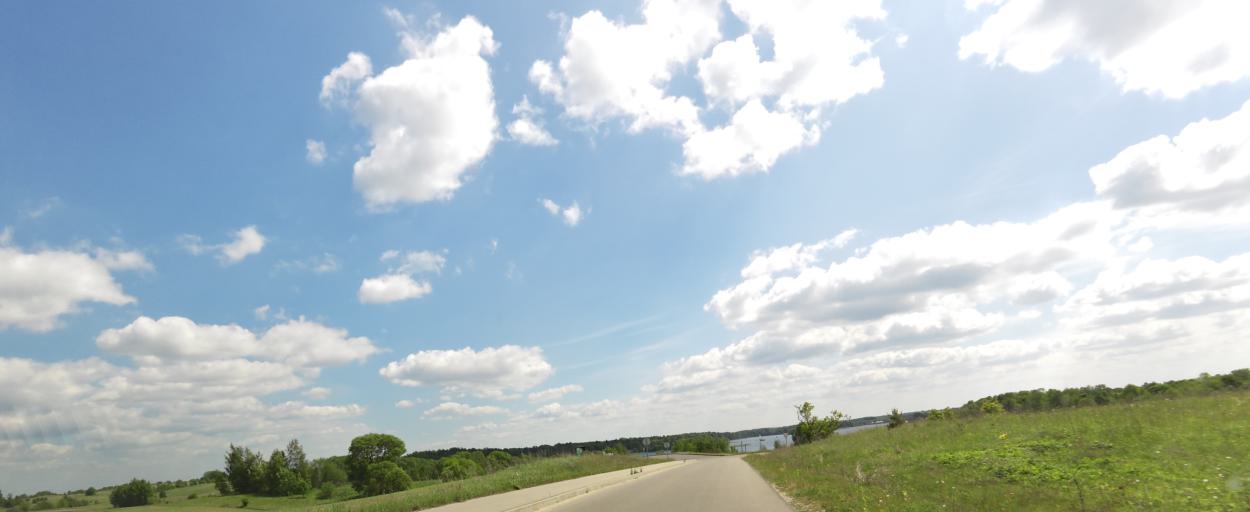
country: LT
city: Trakai
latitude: 54.6740
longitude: 24.9303
